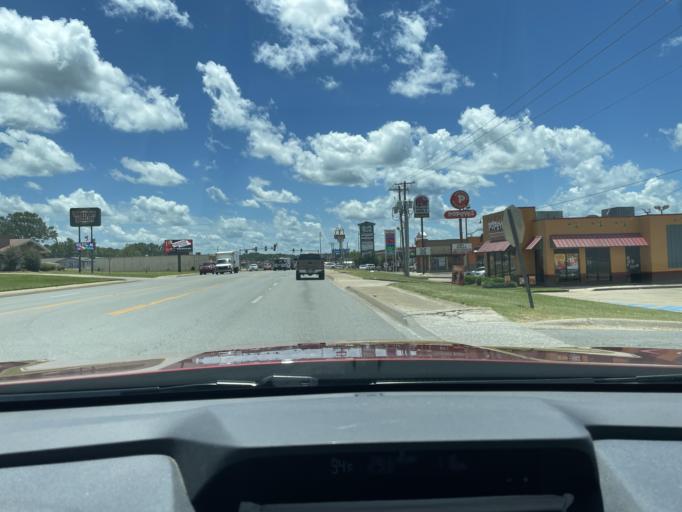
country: US
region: Arkansas
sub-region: Drew County
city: Monticello
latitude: 33.6378
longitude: -91.8015
